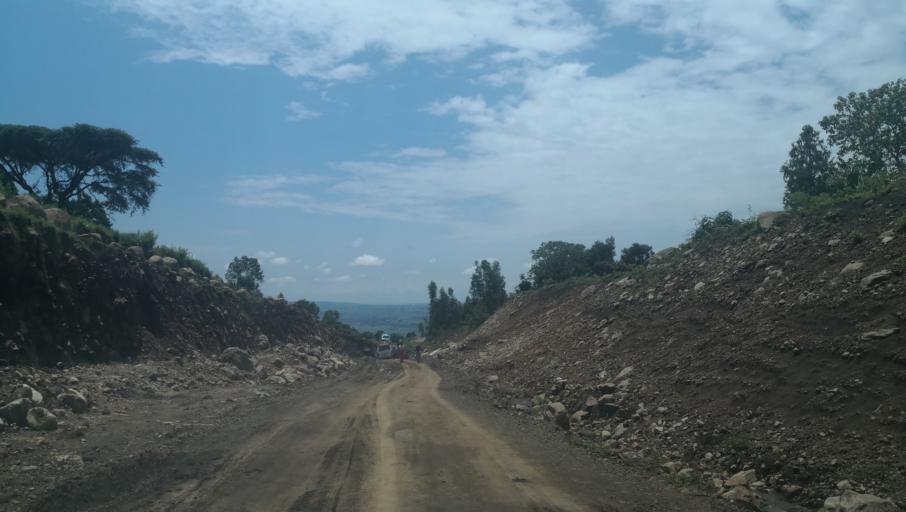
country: ET
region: Southern Nations, Nationalities, and People's Region
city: Butajira
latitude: 8.2751
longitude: 38.4836
